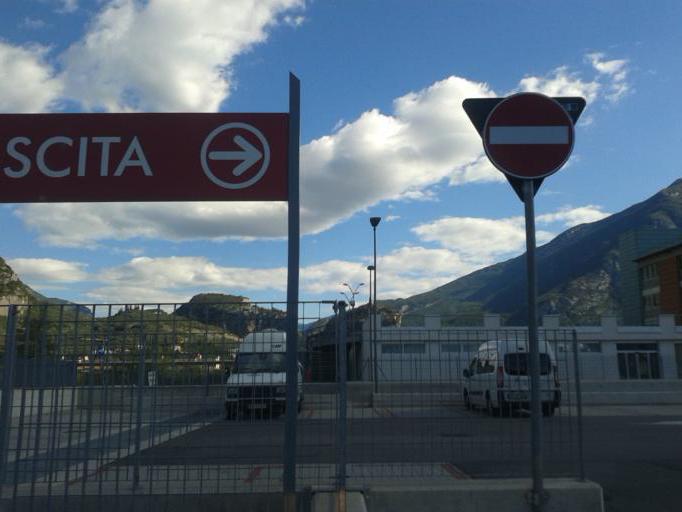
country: IT
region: Trentino-Alto Adige
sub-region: Provincia di Trento
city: Arco
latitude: 45.9107
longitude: 10.8711
